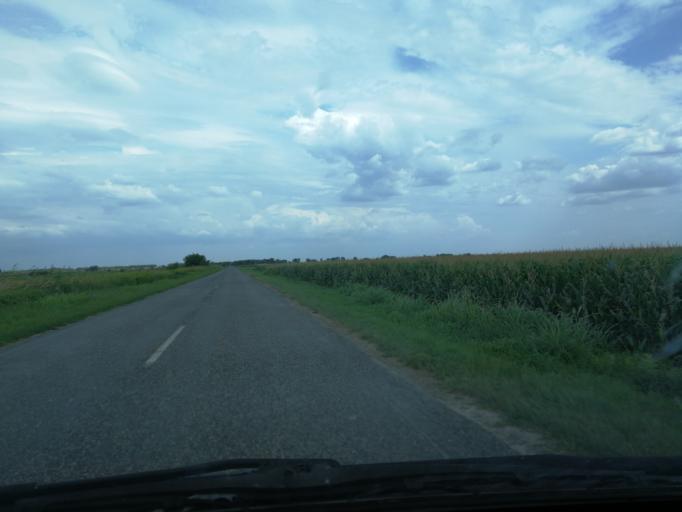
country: HU
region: Bacs-Kiskun
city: Batya
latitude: 46.4476
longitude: 18.9806
